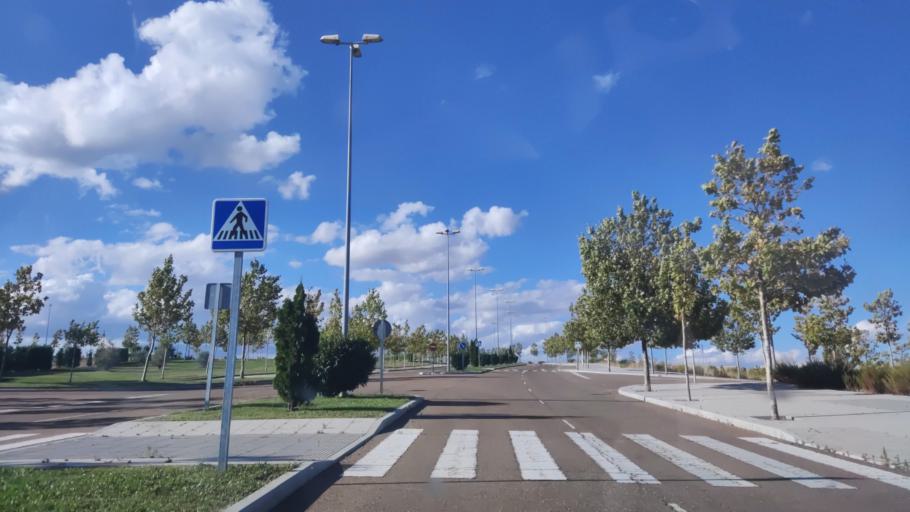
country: ES
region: Castille and Leon
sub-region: Provincia de Salamanca
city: Salamanca
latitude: 40.9693
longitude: -5.6872
